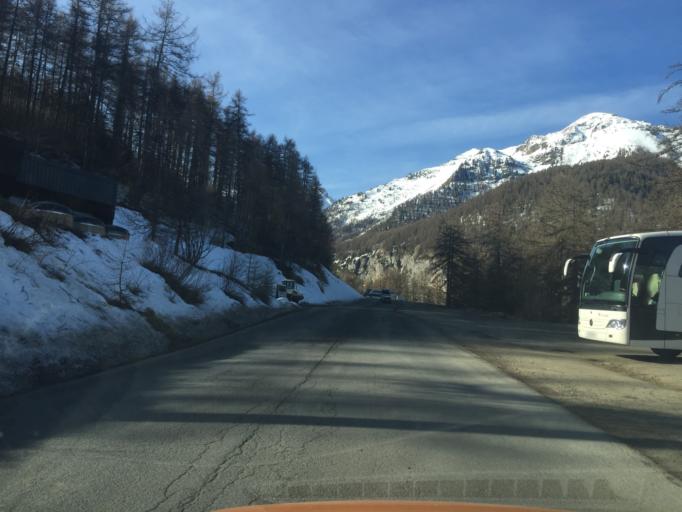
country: FR
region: Provence-Alpes-Cote d'Azur
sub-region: Departement des Hautes-Alpes
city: Embrun
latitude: 44.4878
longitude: 6.5516
